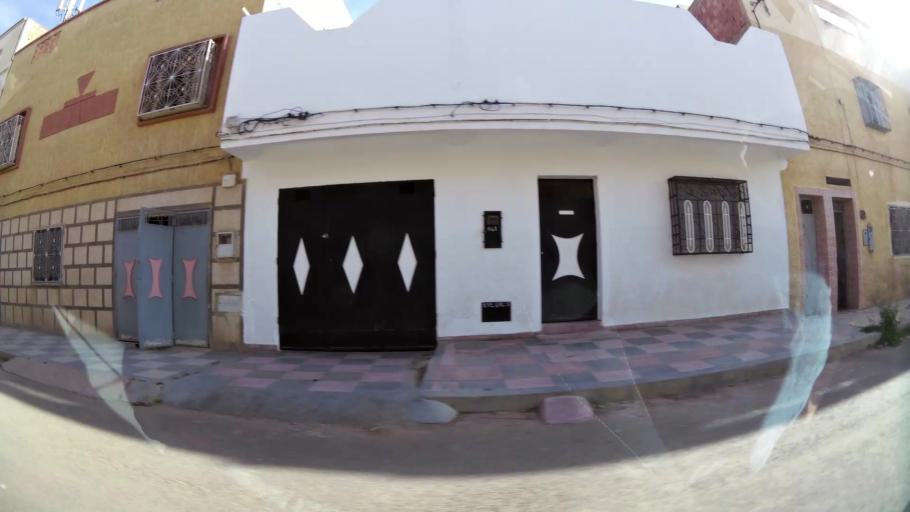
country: MA
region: Oriental
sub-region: Oujda-Angad
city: Oujda
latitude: 34.6736
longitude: -1.8951
